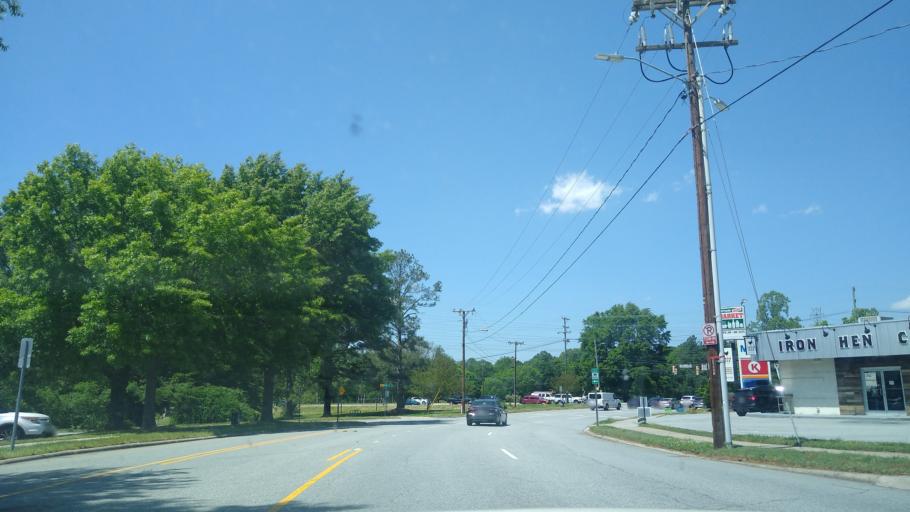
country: US
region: North Carolina
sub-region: Guilford County
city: Greensboro
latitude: 36.0870
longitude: -79.7942
